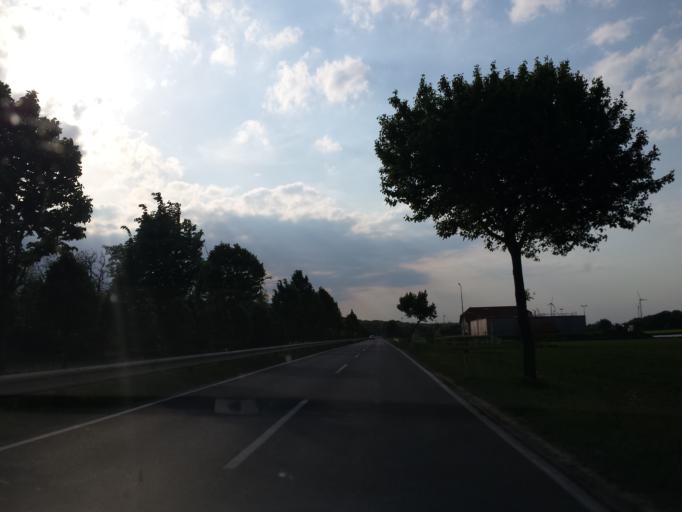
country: AT
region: Lower Austria
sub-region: Politischer Bezirk Ganserndorf
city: Untersiebenbrunn
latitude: 48.2639
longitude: 16.7248
